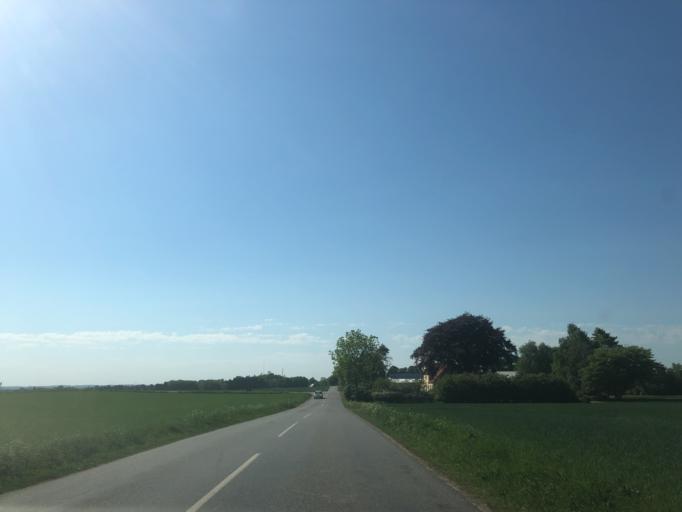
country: DK
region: Zealand
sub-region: Roskilde Kommune
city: Viby
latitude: 55.5720
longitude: 12.0517
